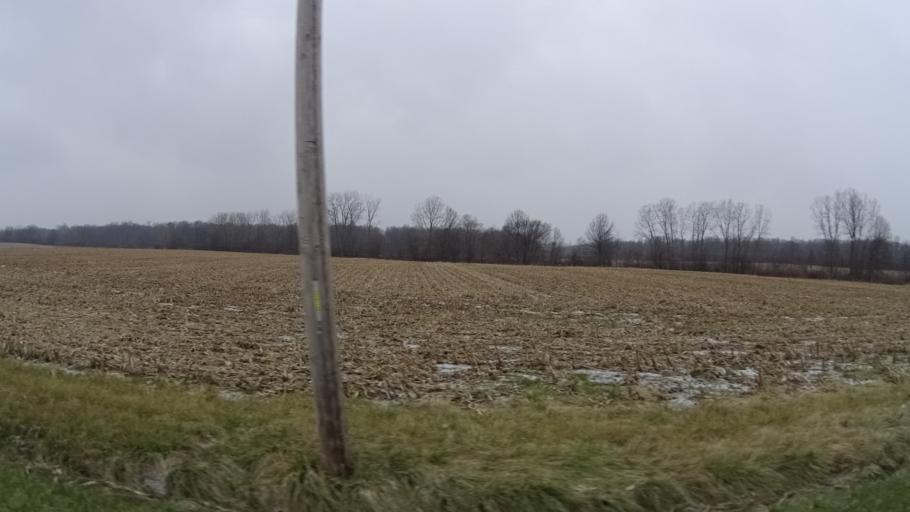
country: US
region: Ohio
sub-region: Lorain County
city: South Amherst
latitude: 41.3250
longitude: -82.2573
